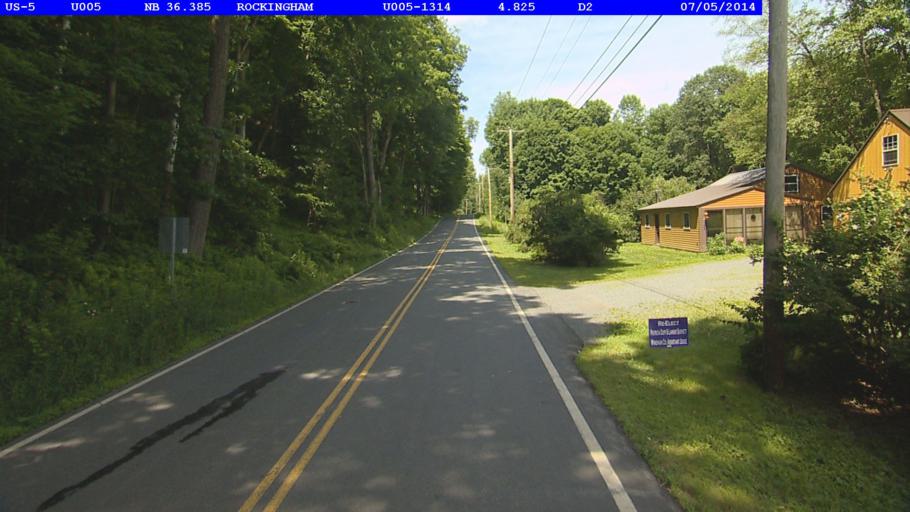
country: US
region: Vermont
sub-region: Windham County
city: Rockingham
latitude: 43.1852
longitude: -72.4512
